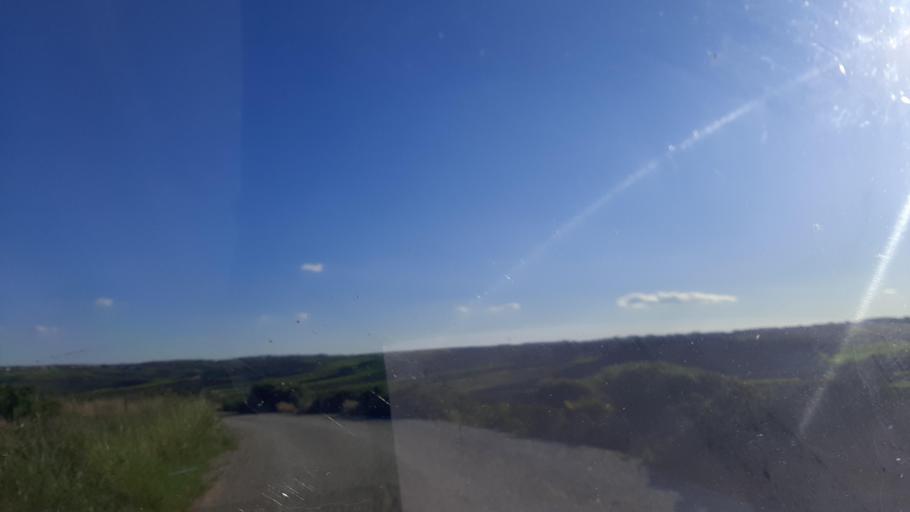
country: TN
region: Nabul
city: El Mida
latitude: 36.8352
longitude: 10.8344
